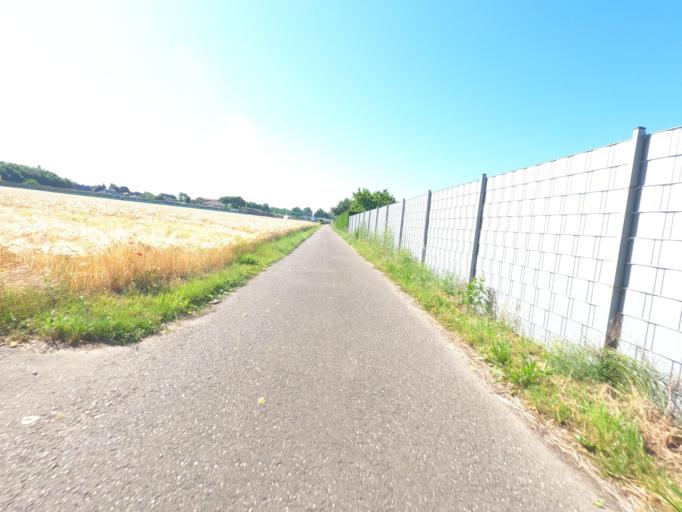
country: DE
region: North Rhine-Westphalia
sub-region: Regierungsbezirk Koln
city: Wassenberg
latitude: 51.1008
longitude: 6.1443
